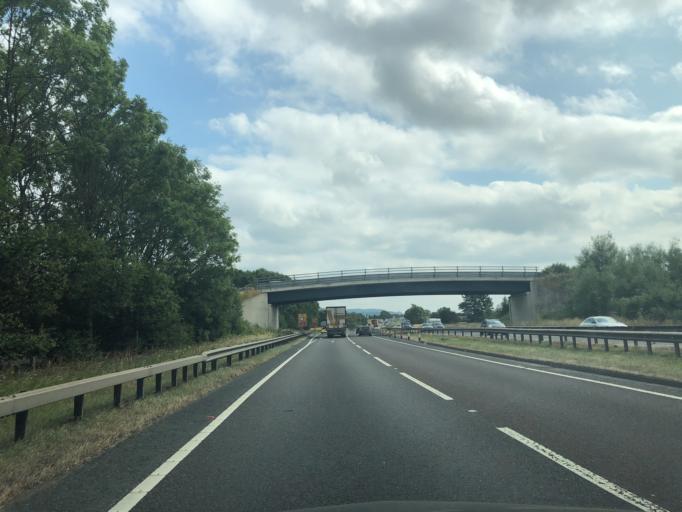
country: GB
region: England
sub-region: Stockton-on-Tees
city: Yarm
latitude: 54.4291
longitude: -1.3207
